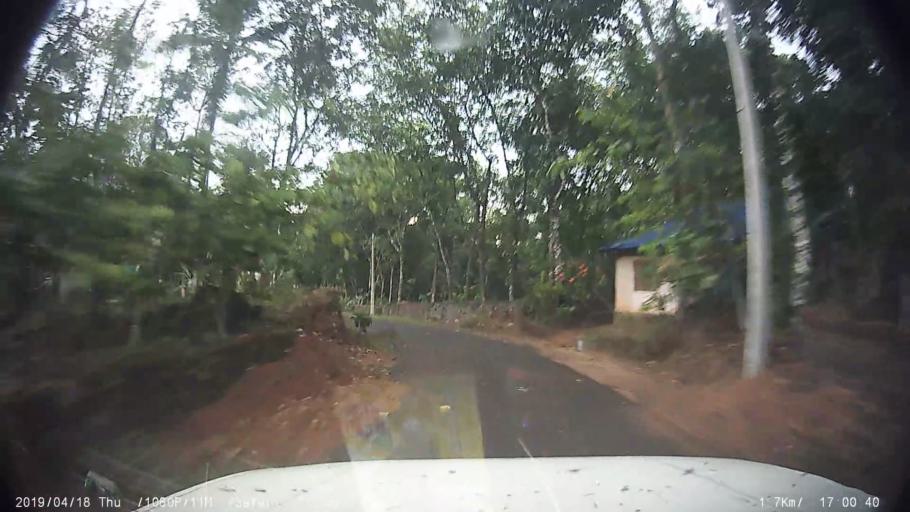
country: IN
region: Kerala
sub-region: Kottayam
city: Palackattumala
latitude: 9.7776
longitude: 76.5820
